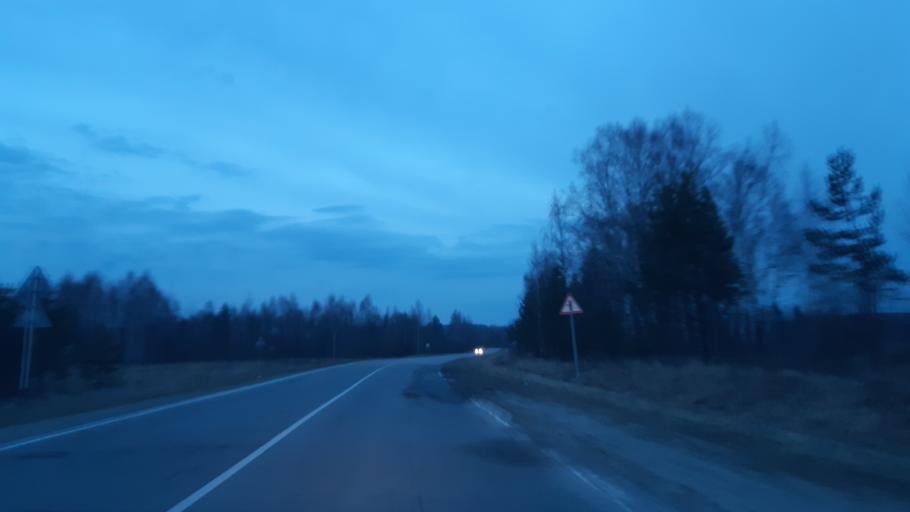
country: RU
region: Vladimir
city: Nikologory
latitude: 56.1747
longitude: 42.0036
